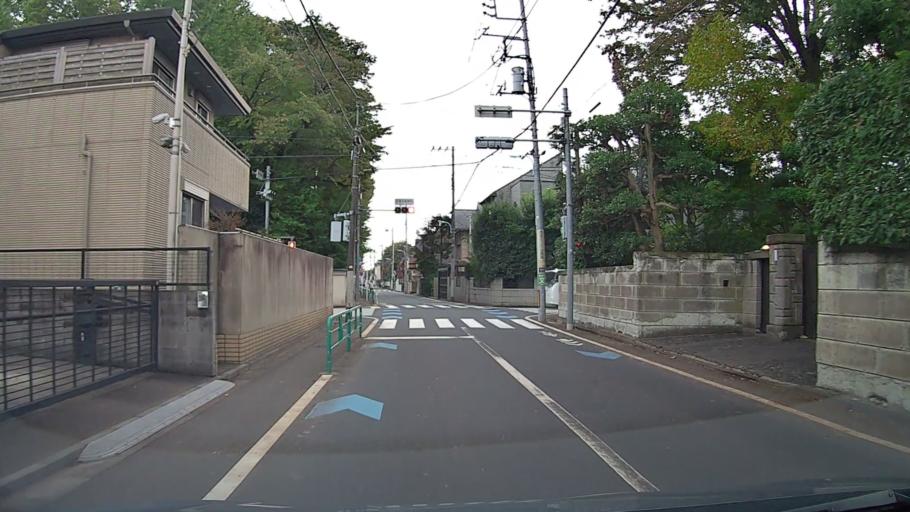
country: JP
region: Tokyo
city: Musashino
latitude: 35.7012
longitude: 139.6087
